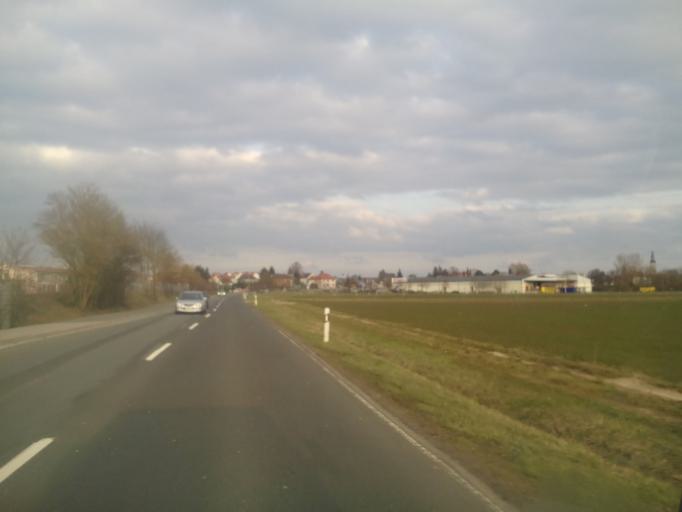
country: DE
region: Bavaria
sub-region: Regierungsbezirk Mittelfranken
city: Hochstadt an der Aisch
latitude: 49.7069
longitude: 10.7936
